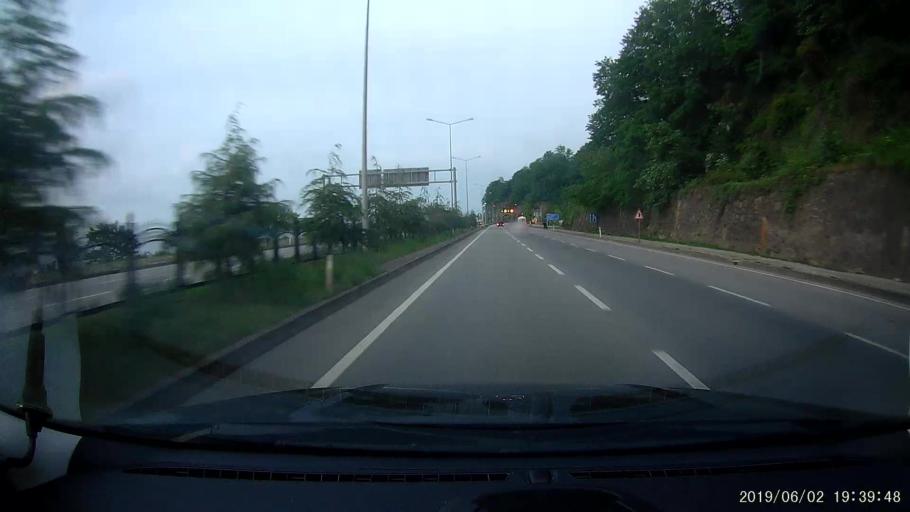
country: TR
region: Giresun
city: Kesap
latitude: 40.9146
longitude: 38.4471
